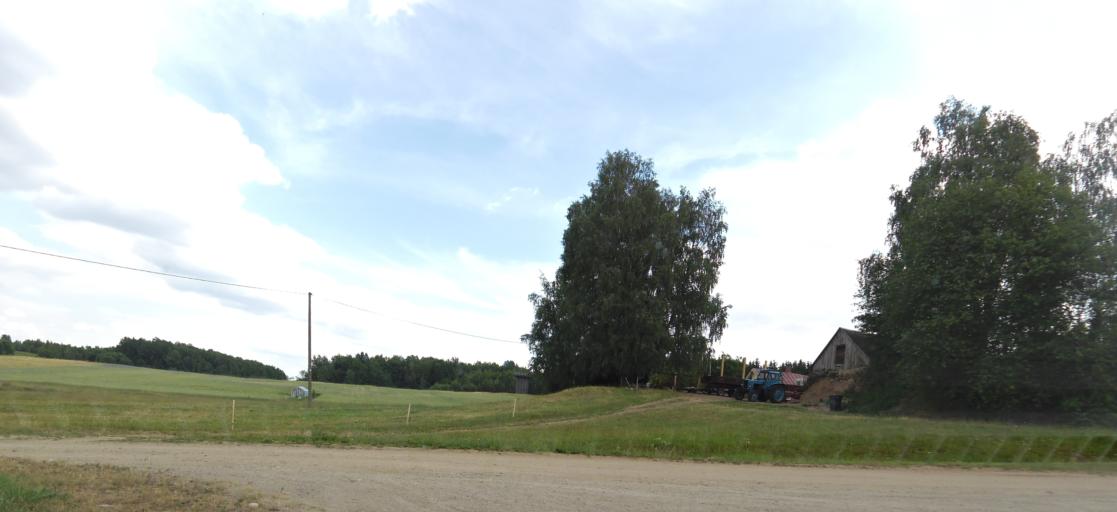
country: LT
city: Skaidiskes
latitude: 54.5285
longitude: 25.6232
